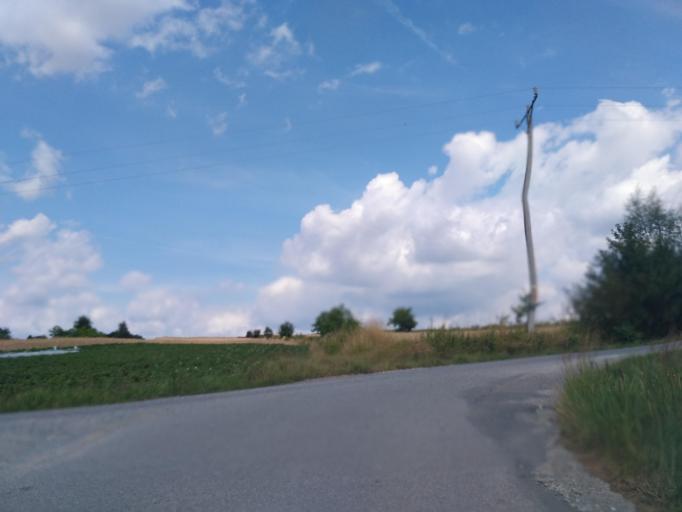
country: PL
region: Subcarpathian Voivodeship
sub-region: Powiat debicki
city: Slotowa
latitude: 49.9472
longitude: 21.2900
